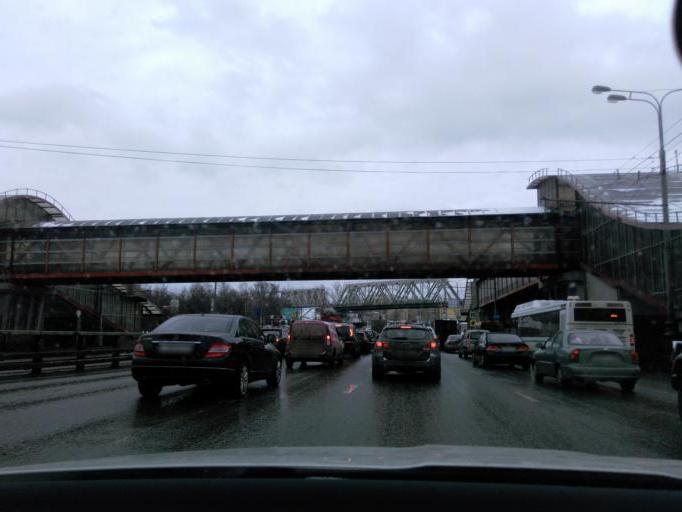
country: RU
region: Moscow
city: Likhobory
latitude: 55.8516
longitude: 37.5650
